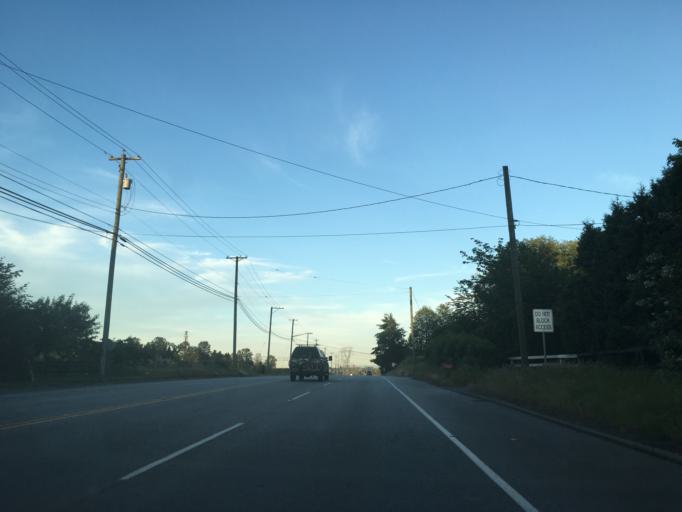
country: US
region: Washington
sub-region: Whatcom County
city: Blaine
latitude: 49.0166
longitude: -122.7515
